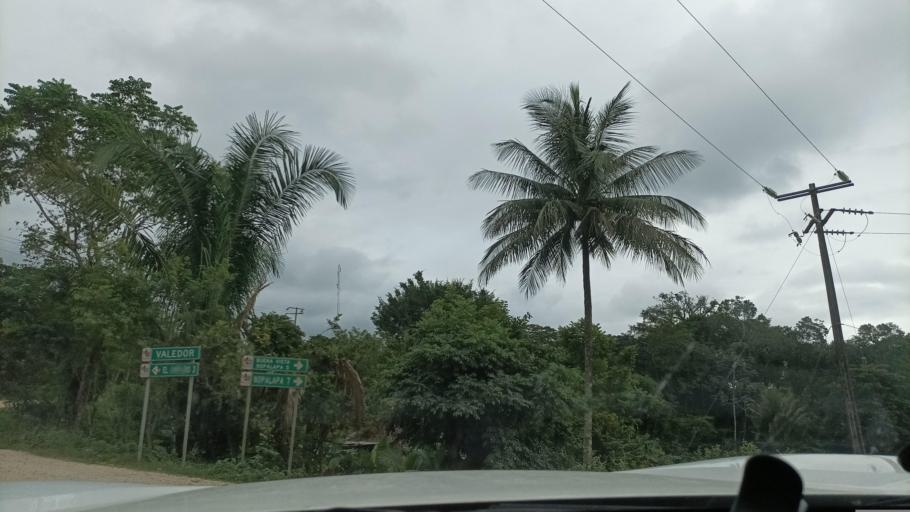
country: MX
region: Veracruz
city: Hidalgotitlan
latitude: 17.7774
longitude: -94.5188
